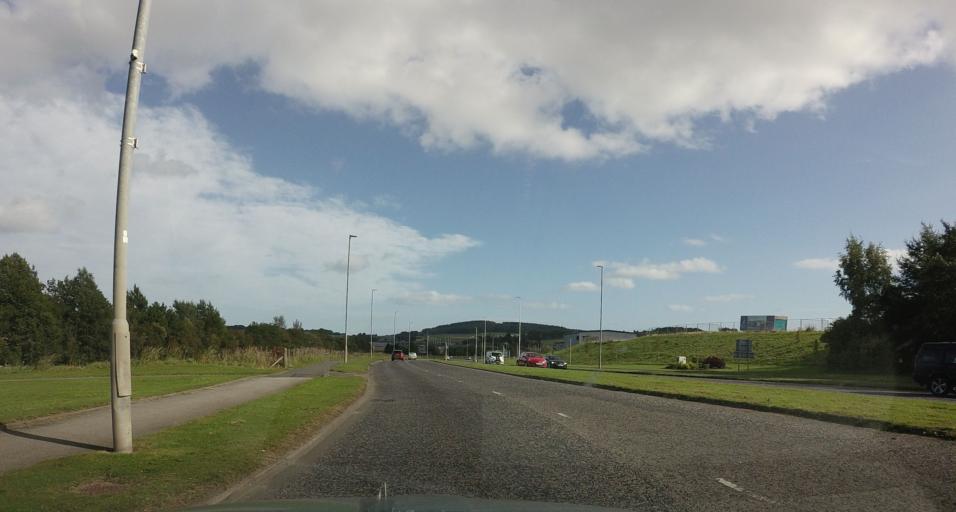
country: GB
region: Scotland
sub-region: Aberdeenshire
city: Westhill
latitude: 57.1503
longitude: -2.2729
